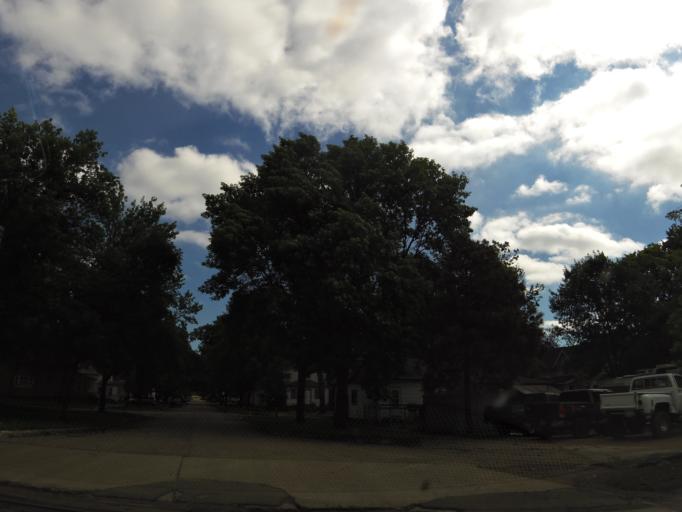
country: US
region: North Dakota
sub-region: Grand Forks County
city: Grand Forks
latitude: 47.9243
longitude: -97.0418
